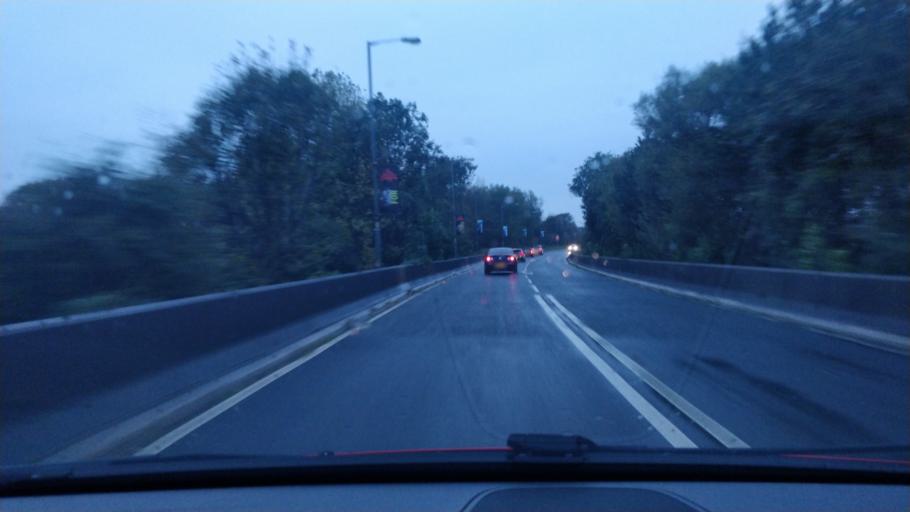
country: GB
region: England
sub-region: Blackpool
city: Blackpool
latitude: 53.7934
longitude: -3.0414
